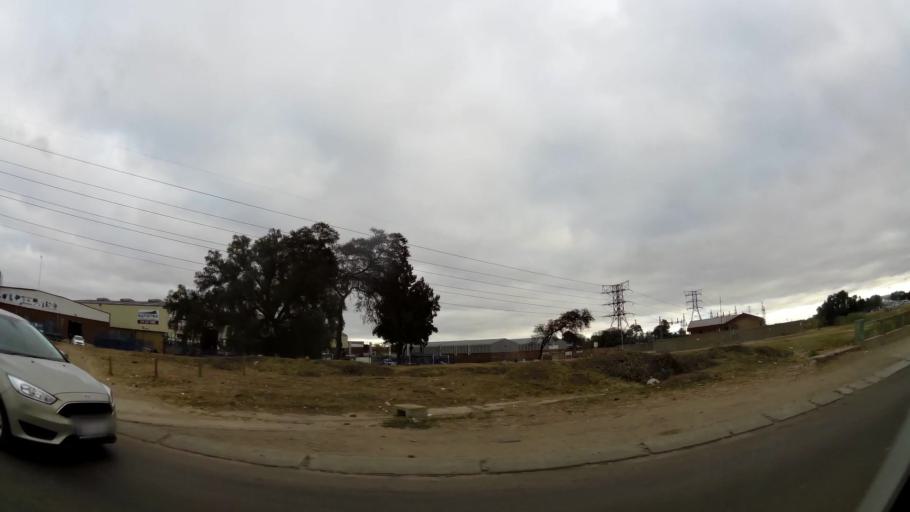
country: ZA
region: Limpopo
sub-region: Capricorn District Municipality
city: Polokwane
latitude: -23.9065
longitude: 29.4418
